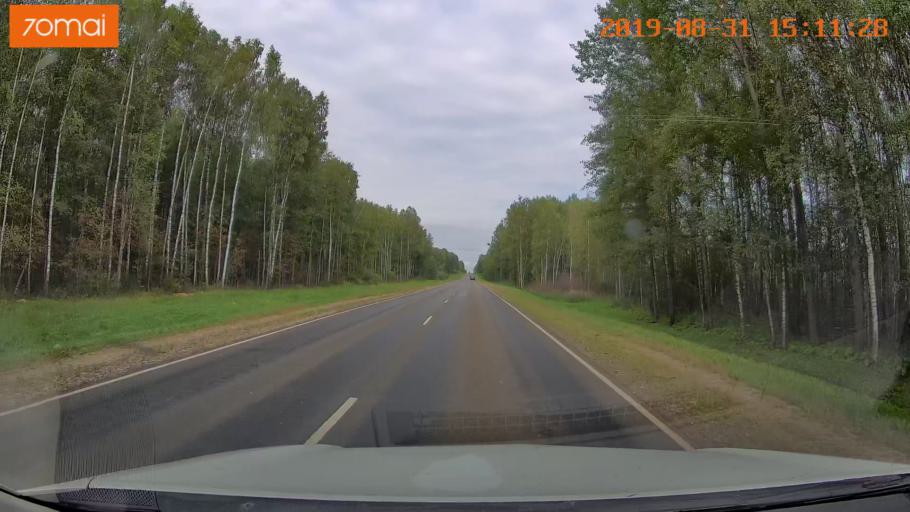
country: RU
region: Kaluga
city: Spas-Demensk
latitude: 54.4227
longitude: 34.2443
